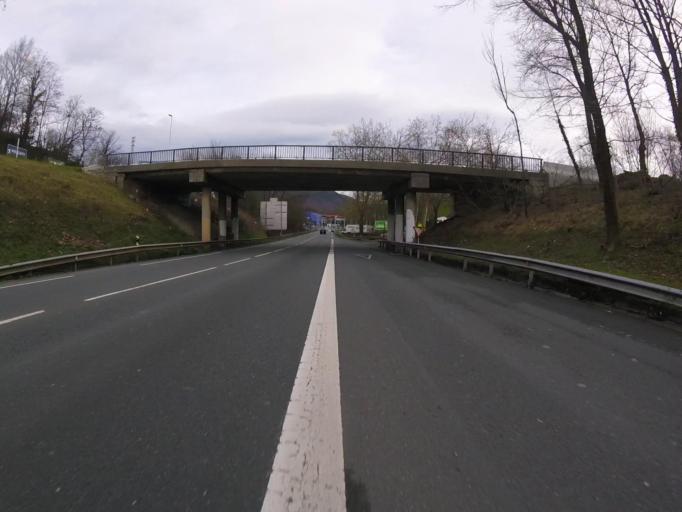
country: ES
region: Basque Country
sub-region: Provincia de Guipuzcoa
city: Lezo
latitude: 43.3152
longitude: -1.8751
